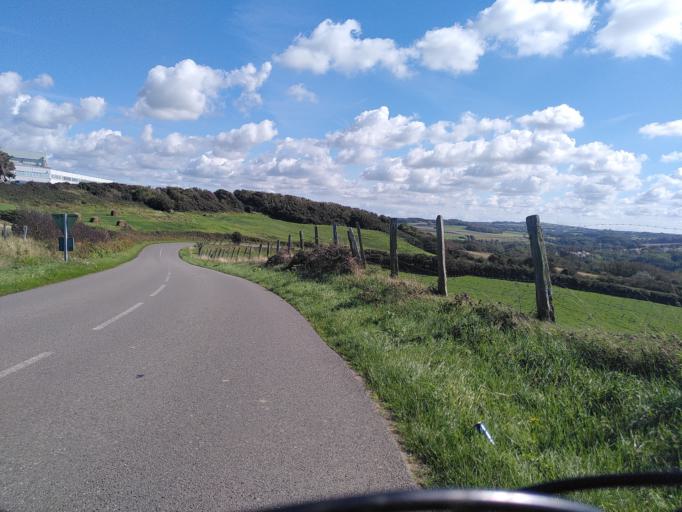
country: FR
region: Nord-Pas-de-Calais
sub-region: Departement du Pas-de-Calais
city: Wimille
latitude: 50.7727
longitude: 1.6296
